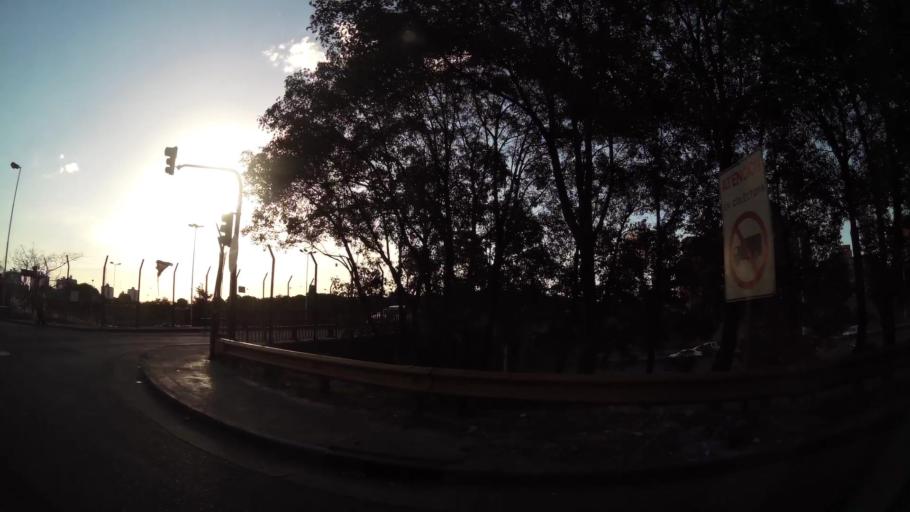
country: AR
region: Buenos Aires F.D.
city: Villa Lugano
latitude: -34.6950
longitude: -58.4913
